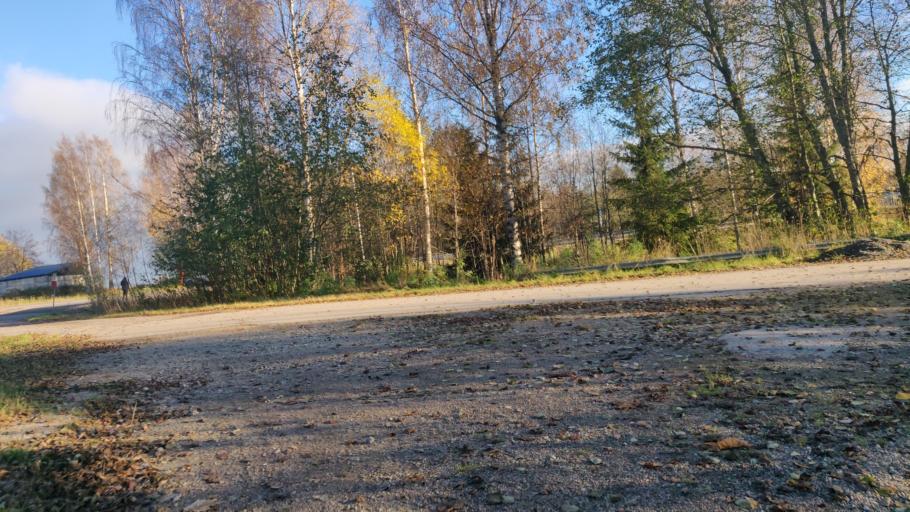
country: SE
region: Vaesternorrland
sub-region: Sundsvalls Kommun
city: Njurundabommen
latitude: 62.2727
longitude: 17.3729
